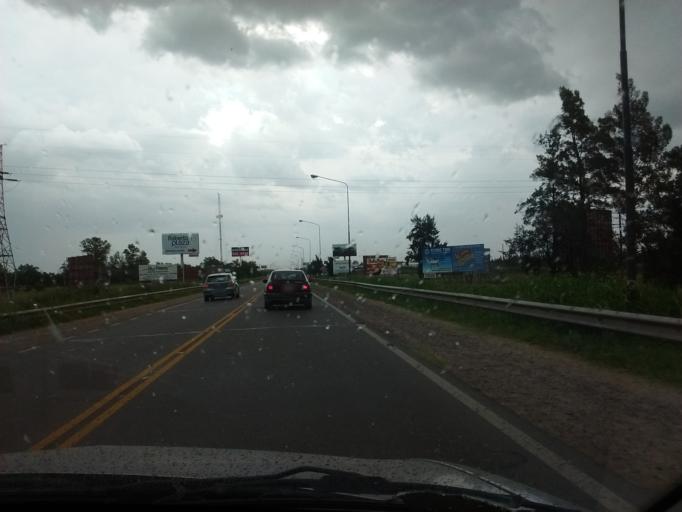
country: AR
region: Santa Fe
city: Funes
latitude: -32.9250
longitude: -60.7668
